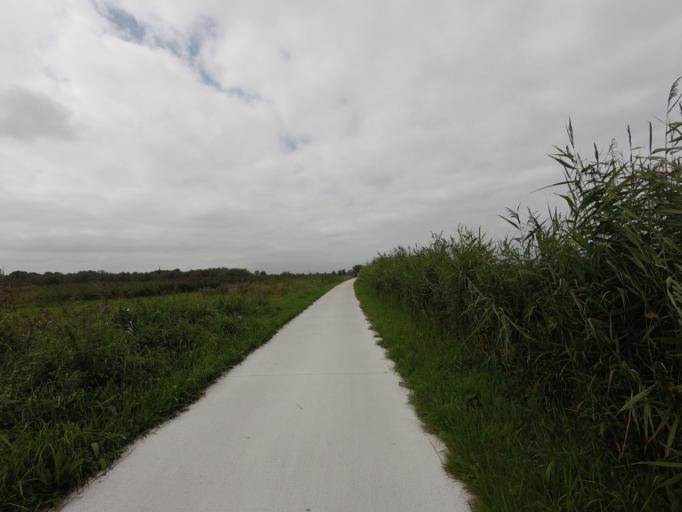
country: NL
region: Overijssel
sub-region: Gemeente Steenwijkerland
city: Oldemarkt
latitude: 52.8043
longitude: 5.9470
